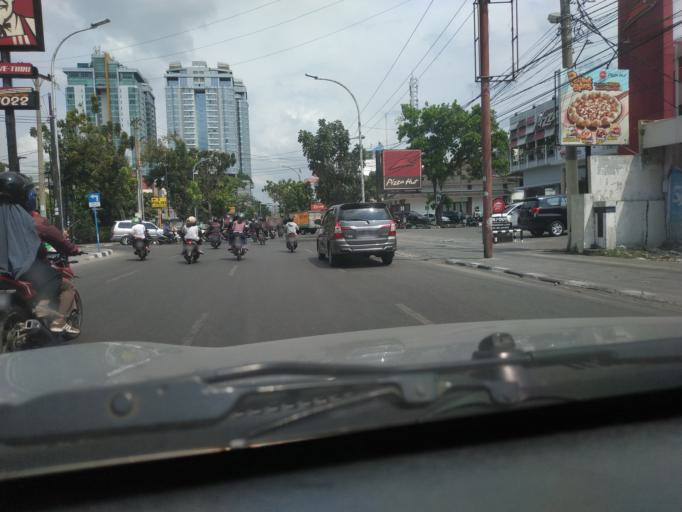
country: ID
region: North Sumatra
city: Medan
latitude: 3.5844
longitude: 98.6641
